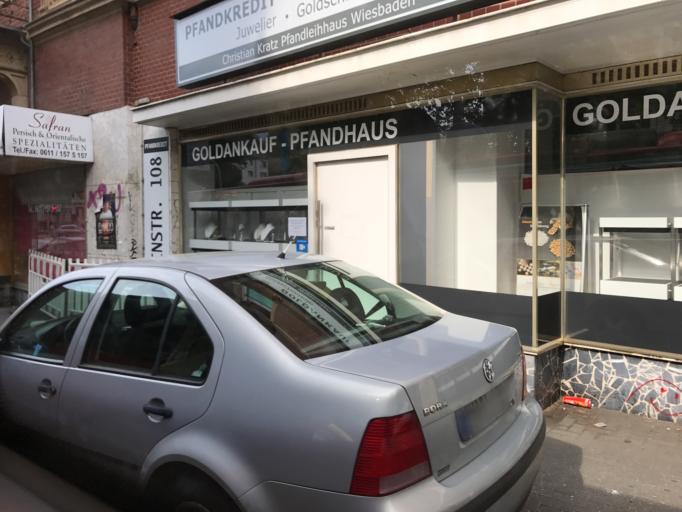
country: DE
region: Hesse
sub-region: Regierungsbezirk Darmstadt
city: Wiesbaden
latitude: 50.0766
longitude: 8.2303
